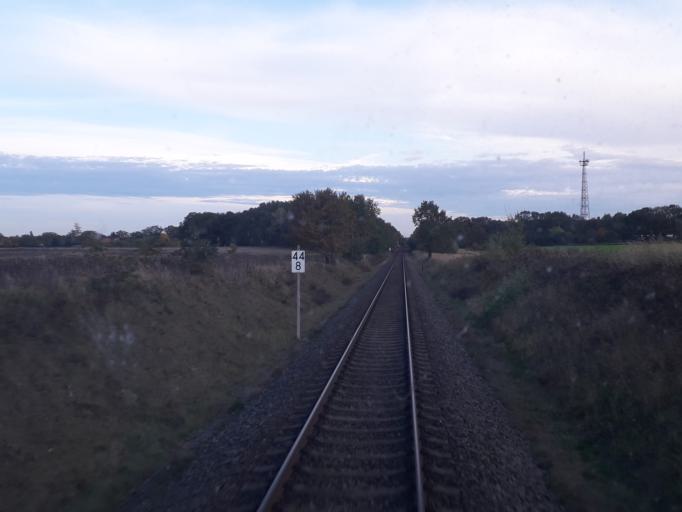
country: DE
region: Brandenburg
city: Walsleben
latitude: 53.0006
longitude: 12.6214
